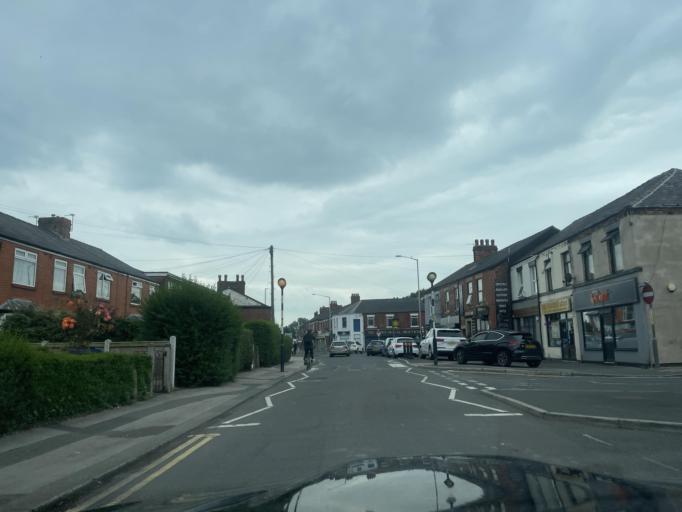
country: GB
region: England
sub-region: Lancashire
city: Leyland
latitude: 53.6897
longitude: -2.7166
